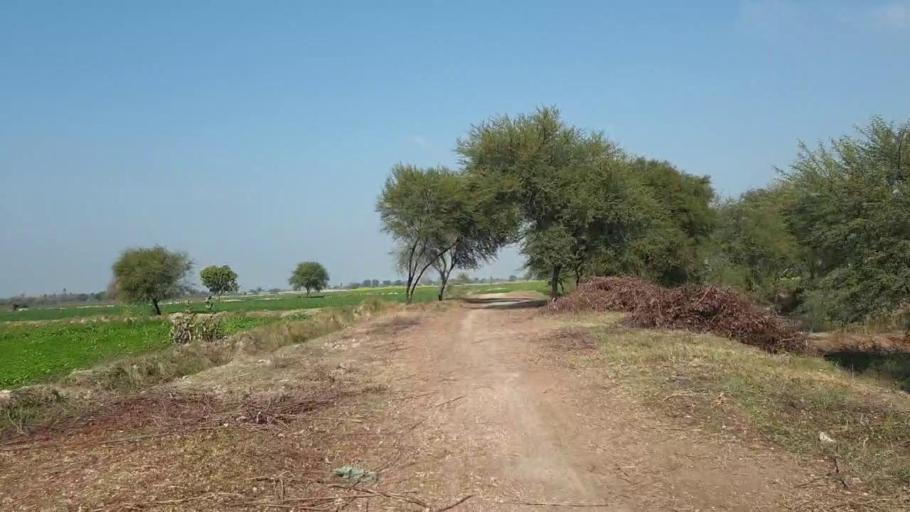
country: PK
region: Sindh
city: Shahdadpur
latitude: 26.0263
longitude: 68.6109
